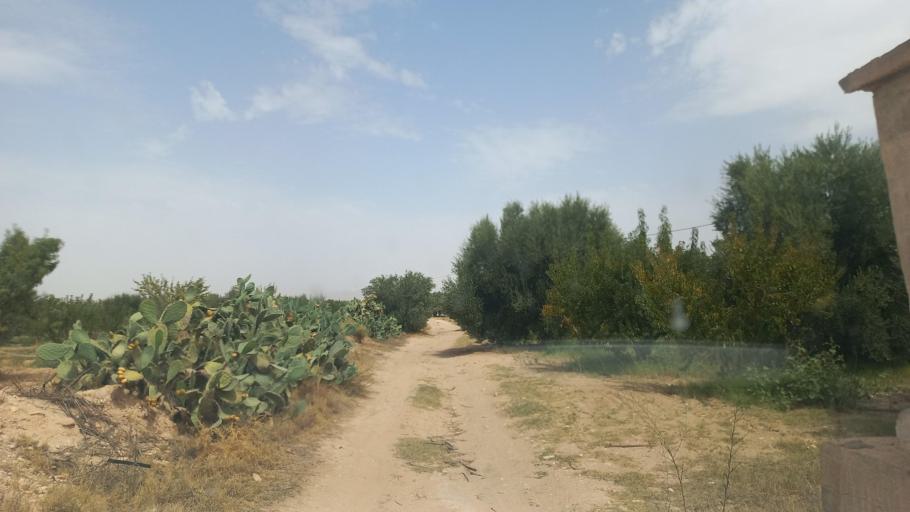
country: TN
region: Al Qasrayn
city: Kasserine
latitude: 35.2608
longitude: 9.0000
